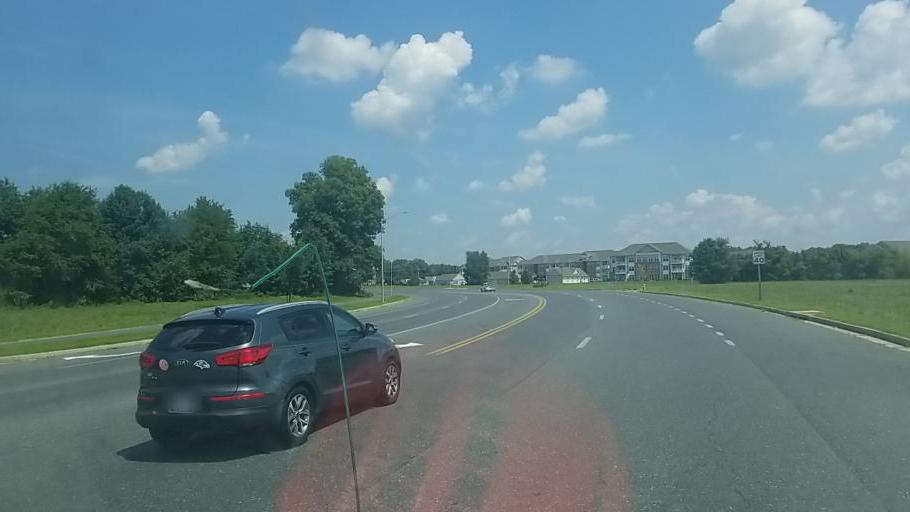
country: US
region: Maryland
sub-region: Wicomico County
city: Salisbury
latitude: 38.3693
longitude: -75.5599
